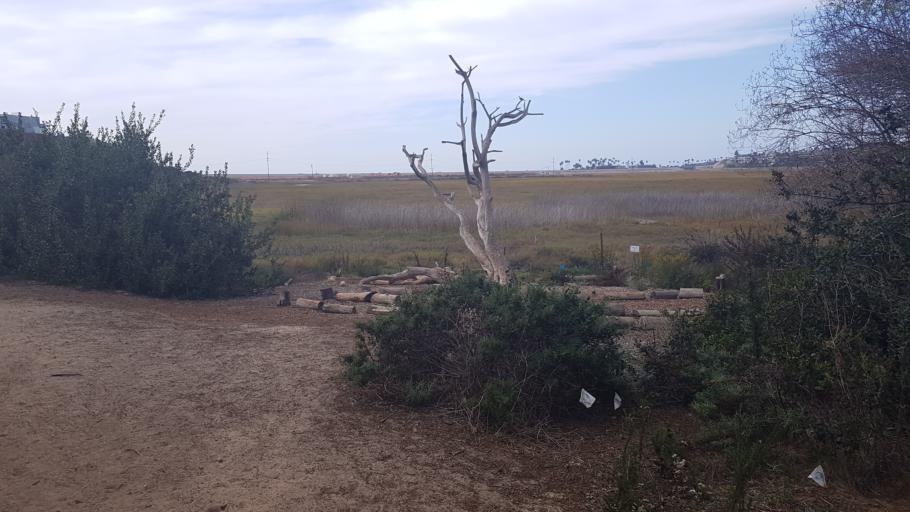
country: US
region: California
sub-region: San Diego County
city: Solana Beach
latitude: 33.0041
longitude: -117.2705
